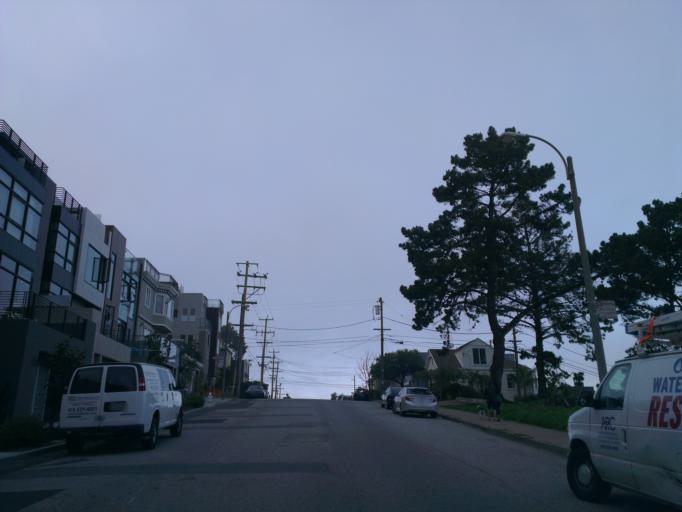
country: US
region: California
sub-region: San Francisco County
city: San Francisco
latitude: 37.7434
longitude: -122.4356
